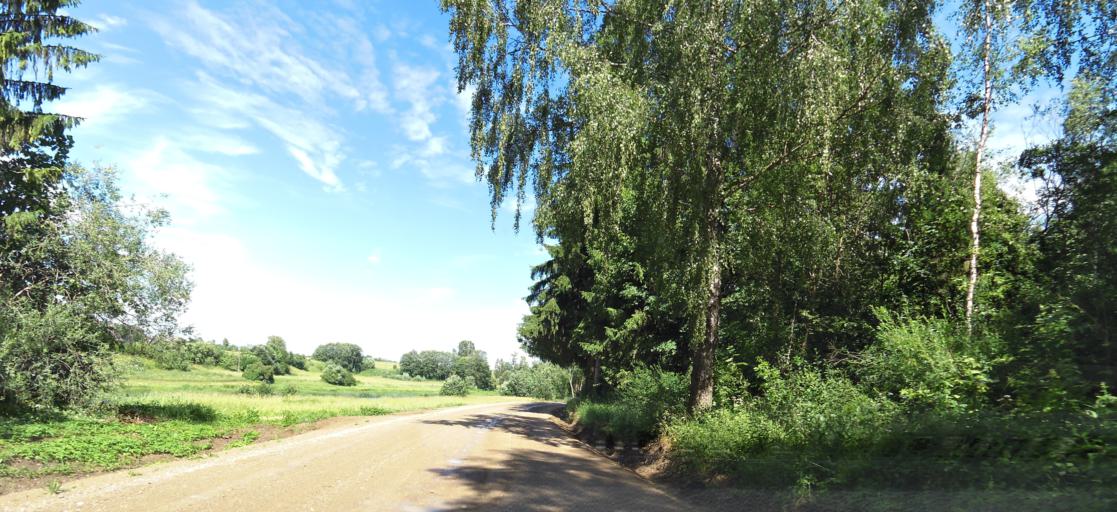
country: LT
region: Panevezys
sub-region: Birzai
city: Birzai
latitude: 56.4058
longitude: 24.7916
